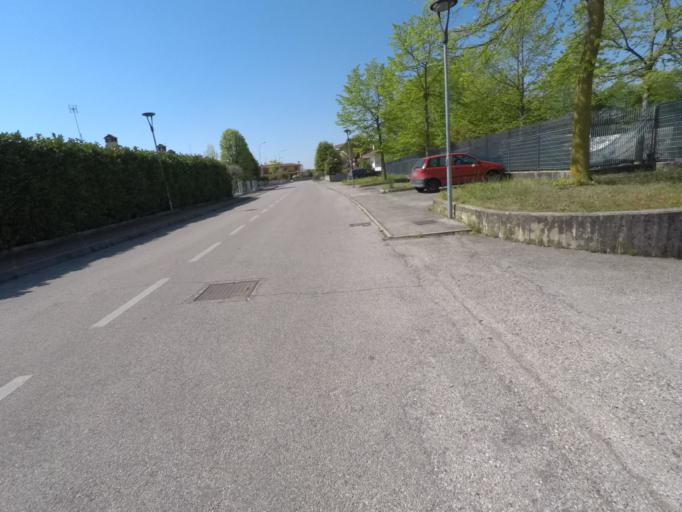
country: IT
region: Friuli Venezia Giulia
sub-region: Provincia di Pordenone
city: Brugnera
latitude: 45.8985
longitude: 12.5344
